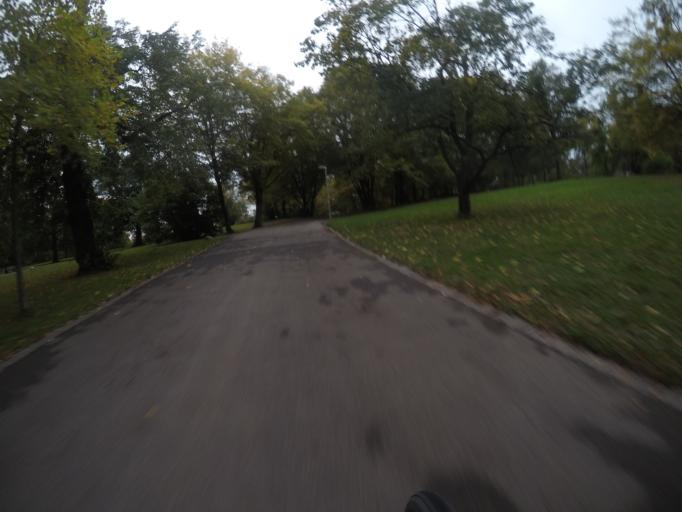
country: DE
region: Baden-Wuerttemberg
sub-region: Regierungsbezirk Stuttgart
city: Stuttgart-Ost
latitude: 48.7934
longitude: 9.2100
